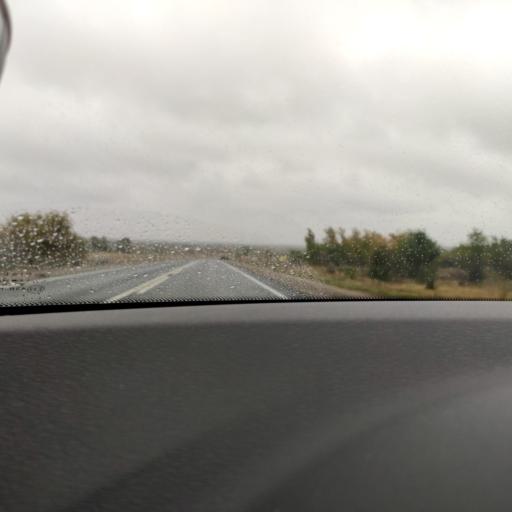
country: RU
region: Samara
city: Mirnyy
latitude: 53.6380
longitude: 50.2328
